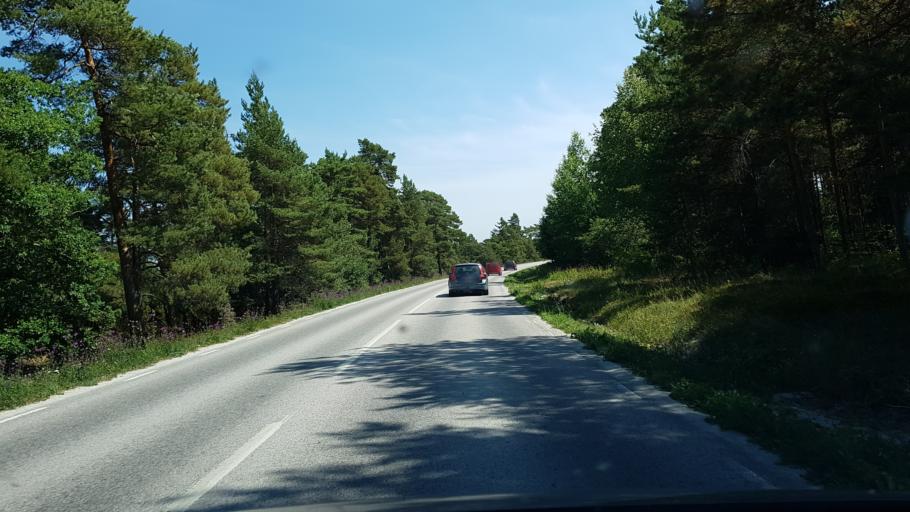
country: SE
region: Gotland
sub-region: Gotland
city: Visby
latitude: 57.6378
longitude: 18.3992
